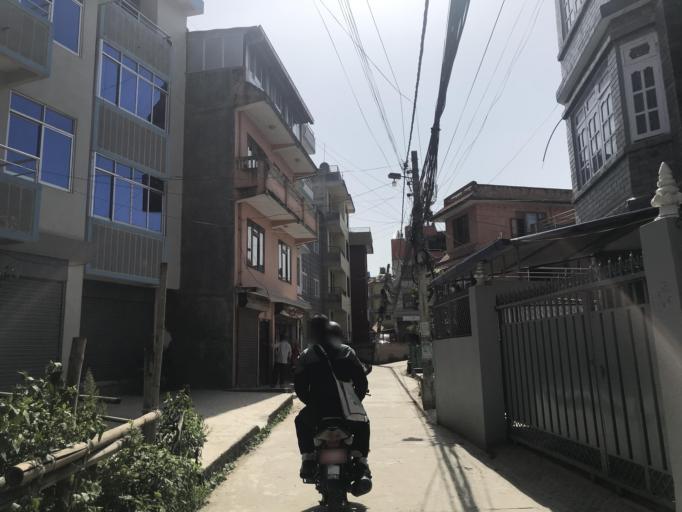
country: NP
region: Central Region
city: Kirtipur
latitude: 27.6811
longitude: 85.2811
